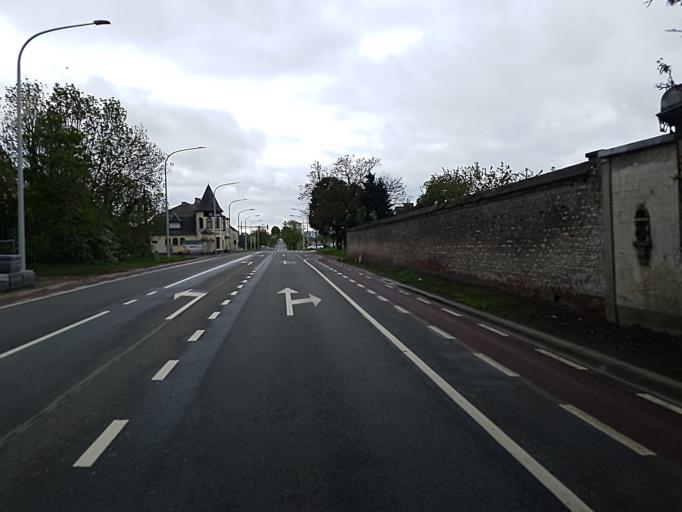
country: BE
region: Wallonia
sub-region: Province du Brabant Wallon
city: Chastre-Villeroux-Blanmont
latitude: 50.6285
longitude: 4.6559
